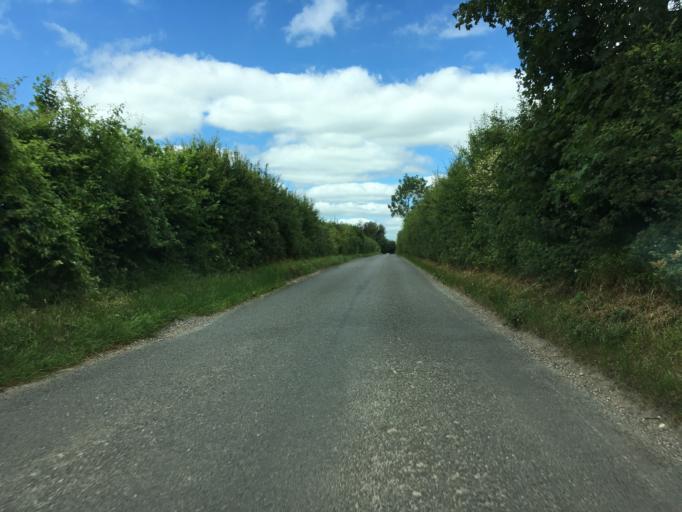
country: GB
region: England
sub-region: Hampshire
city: Overton
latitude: 51.2414
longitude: -1.3523
